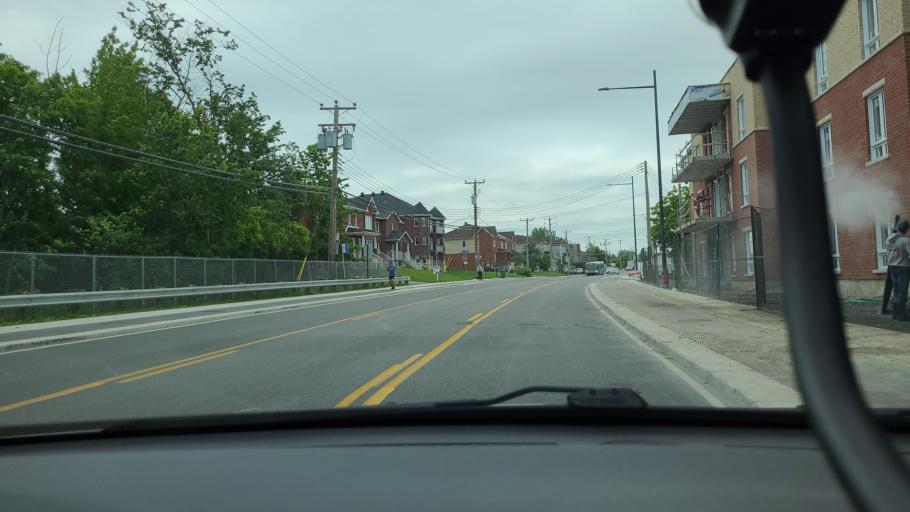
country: CA
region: Quebec
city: Bois-des-Filion
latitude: 45.6503
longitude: -73.7485
